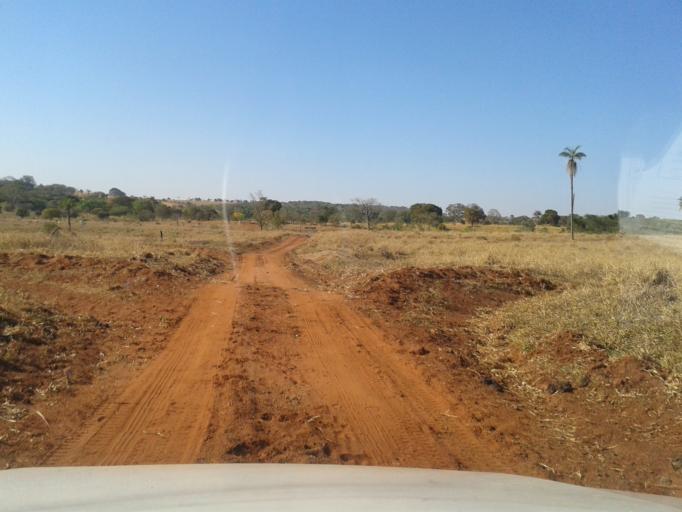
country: BR
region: Minas Gerais
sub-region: Santa Vitoria
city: Santa Vitoria
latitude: -19.0605
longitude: -49.9255
